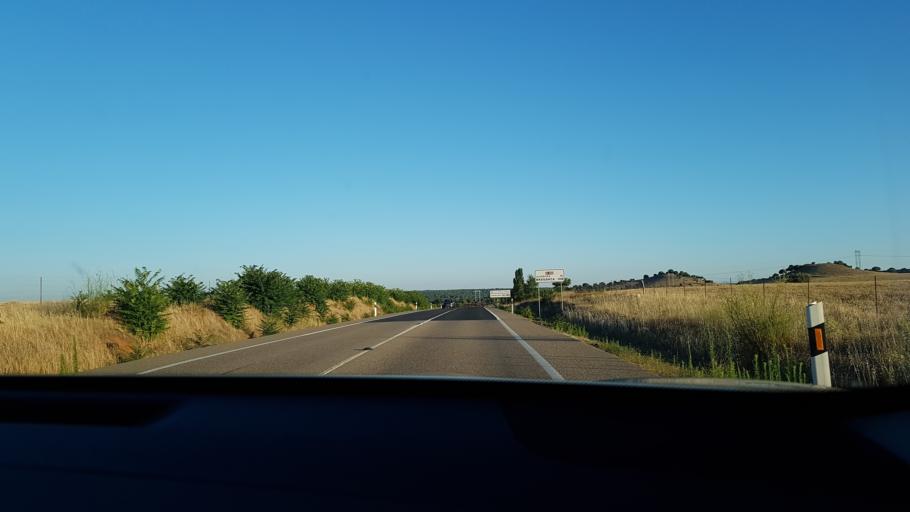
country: ES
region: Castille and Leon
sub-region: Provincia de Zamora
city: Roales
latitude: 41.5264
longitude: -5.8112
